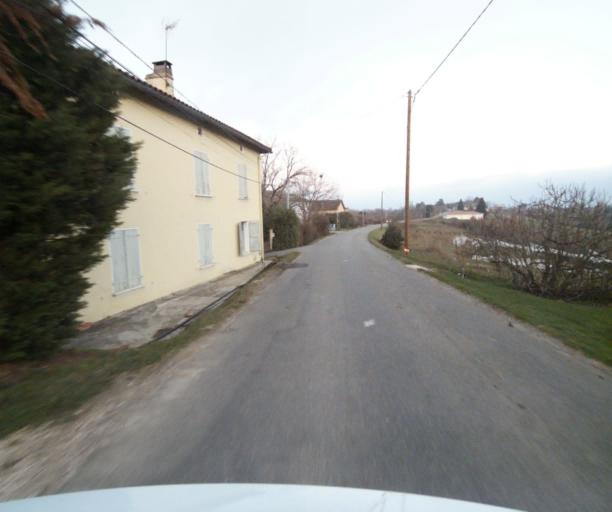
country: FR
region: Midi-Pyrenees
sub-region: Departement du Tarn-et-Garonne
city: Moissac
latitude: 44.1220
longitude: 1.0797
